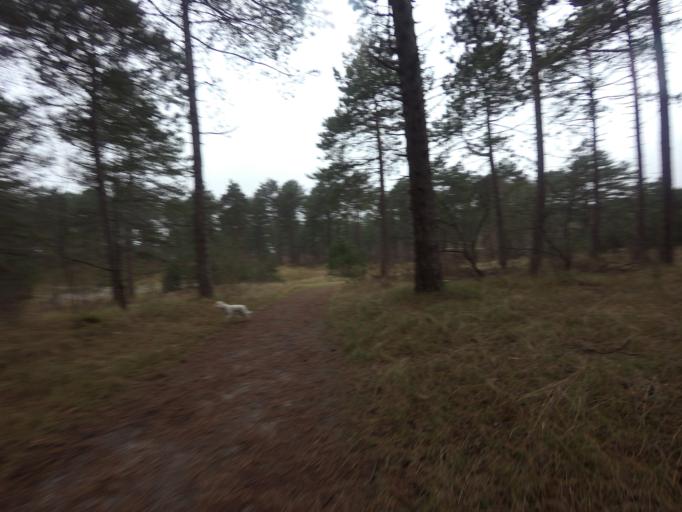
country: NL
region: Zeeland
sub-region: Schouwen-Duiveland
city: Burgh
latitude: 51.6897
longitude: 3.7023
